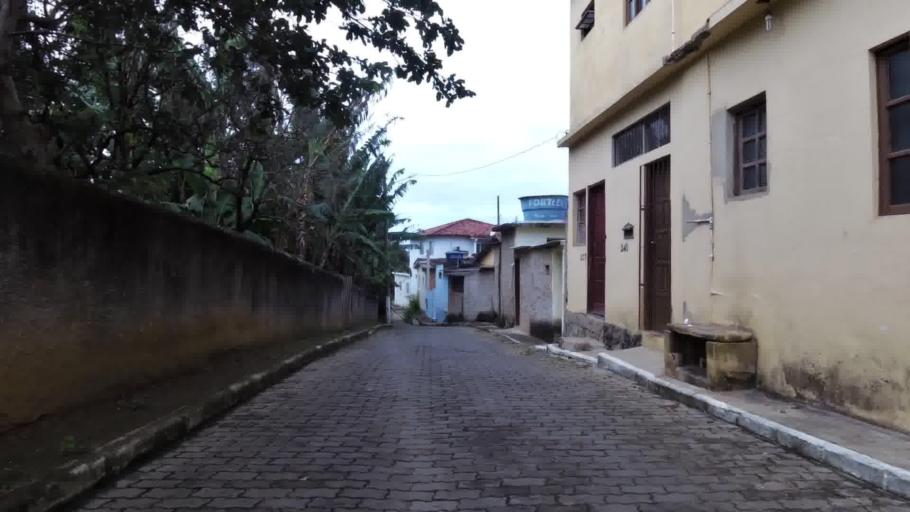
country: BR
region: Espirito Santo
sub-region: Piuma
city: Piuma
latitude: -20.8025
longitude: -40.6523
